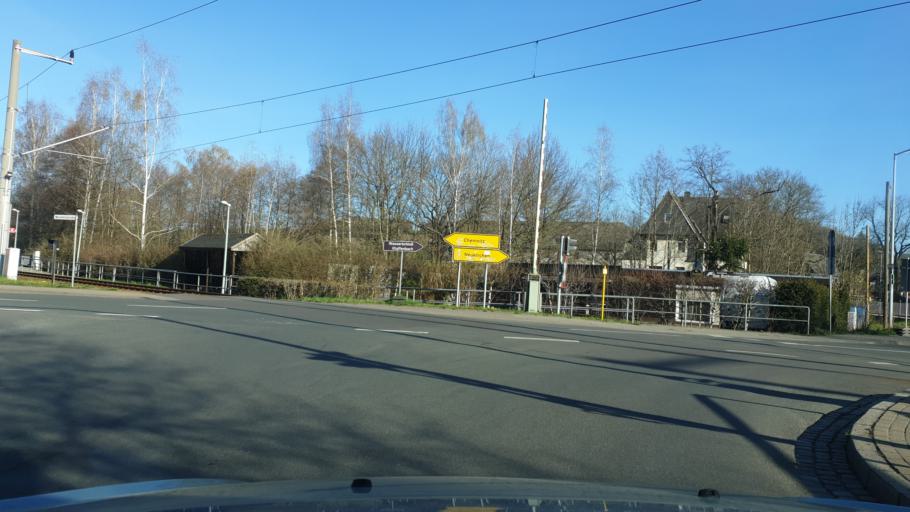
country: DE
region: Saxony
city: Neukirchen
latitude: 50.7723
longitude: 12.9024
